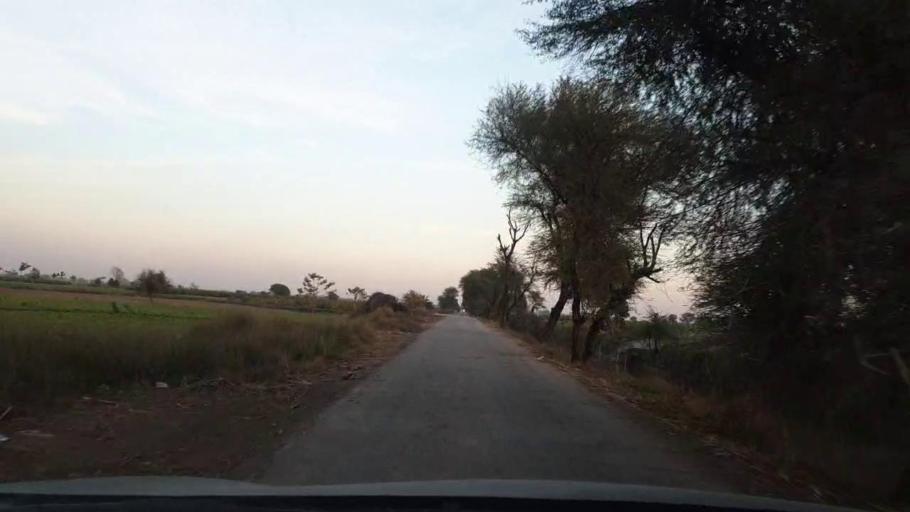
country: PK
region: Sindh
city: Tando Allahyar
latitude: 25.5942
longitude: 68.7061
